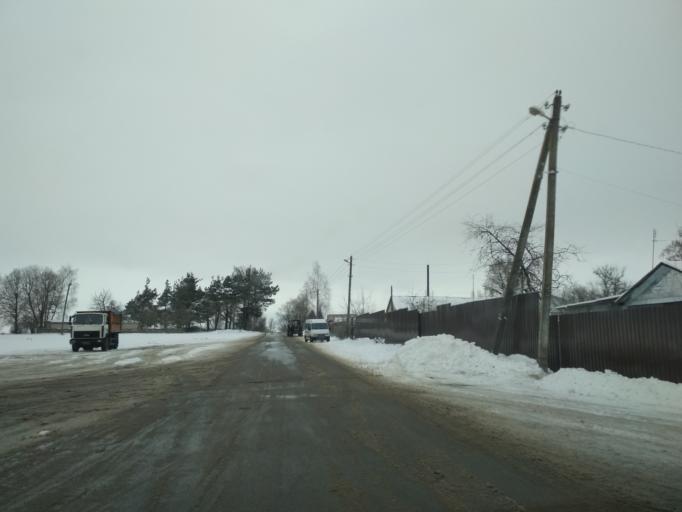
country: BY
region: Minsk
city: Mar''ina Horka
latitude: 53.4908
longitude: 28.1456
